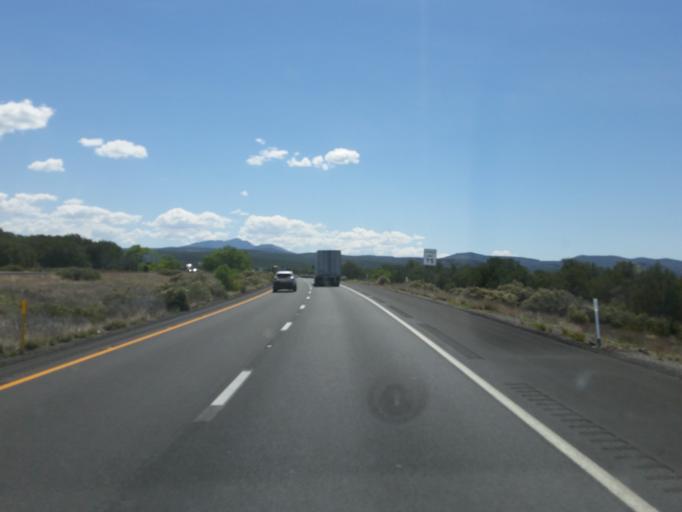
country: US
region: Arizona
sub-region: Coconino County
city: Williams
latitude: 35.2147
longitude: -112.4311
